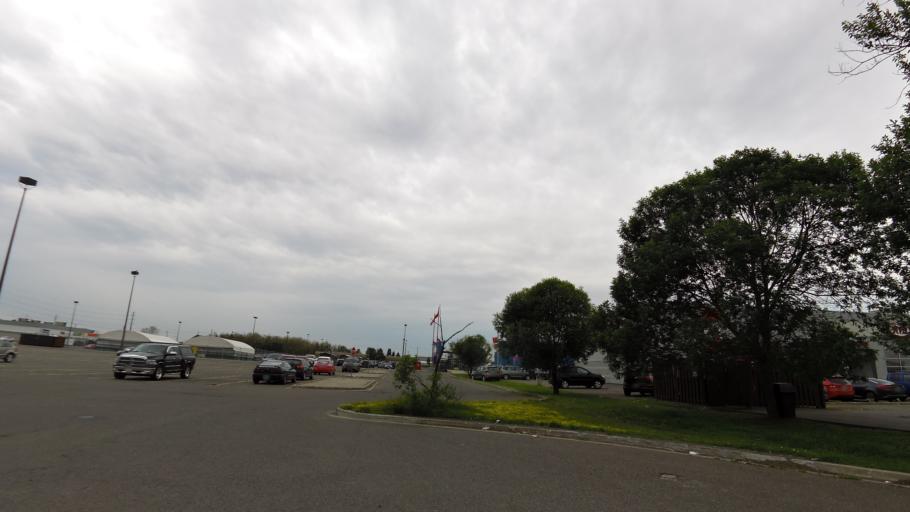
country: CA
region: Ontario
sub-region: Thunder Bay District
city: Thunder Bay
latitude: 48.4086
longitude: -89.2462
